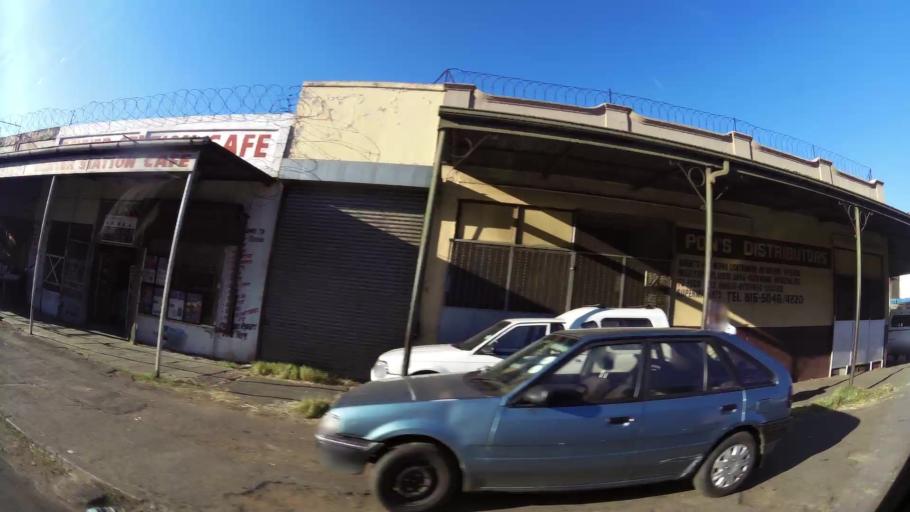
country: ZA
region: Gauteng
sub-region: City of Johannesburg Metropolitan Municipality
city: Johannesburg
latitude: -26.2065
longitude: 28.0977
